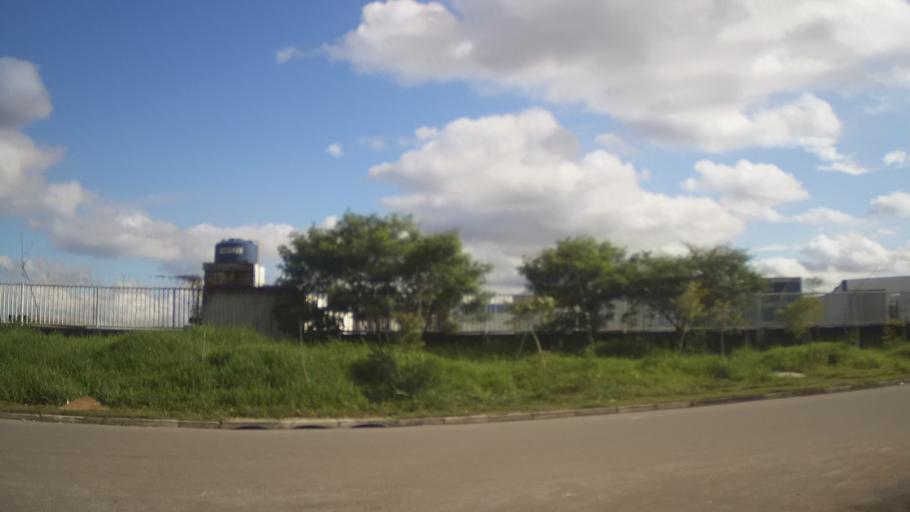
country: BR
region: Sao Paulo
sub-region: Guarulhos
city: Guarulhos
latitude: -23.4685
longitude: -46.4786
